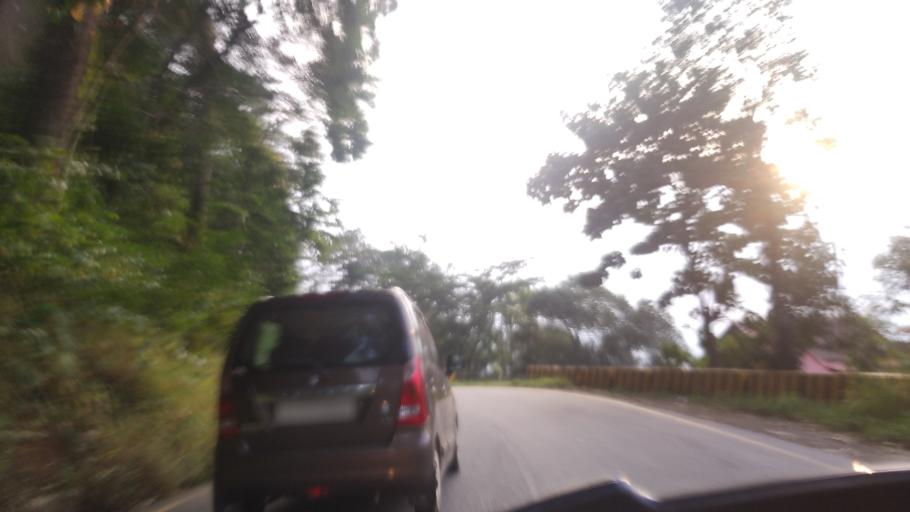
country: IN
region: Kerala
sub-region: Wayanad
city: Kalpetta
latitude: 11.5007
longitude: 76.0224
